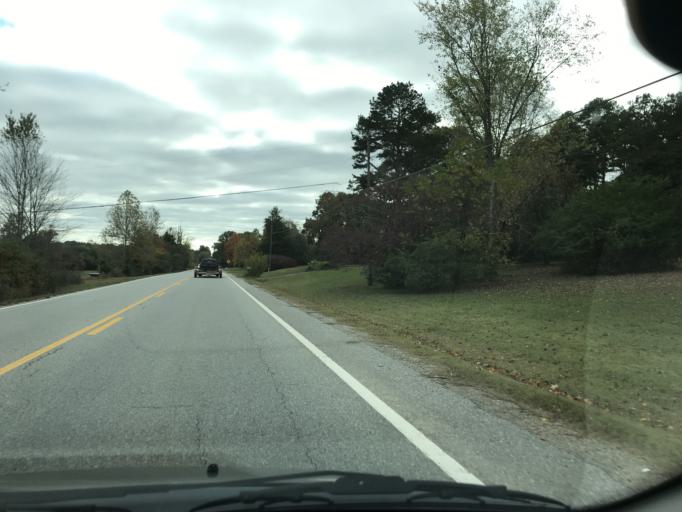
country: US
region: Tennessee
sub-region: Hamilton County
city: Lakesite
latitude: 35.2390
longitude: -85.0126
